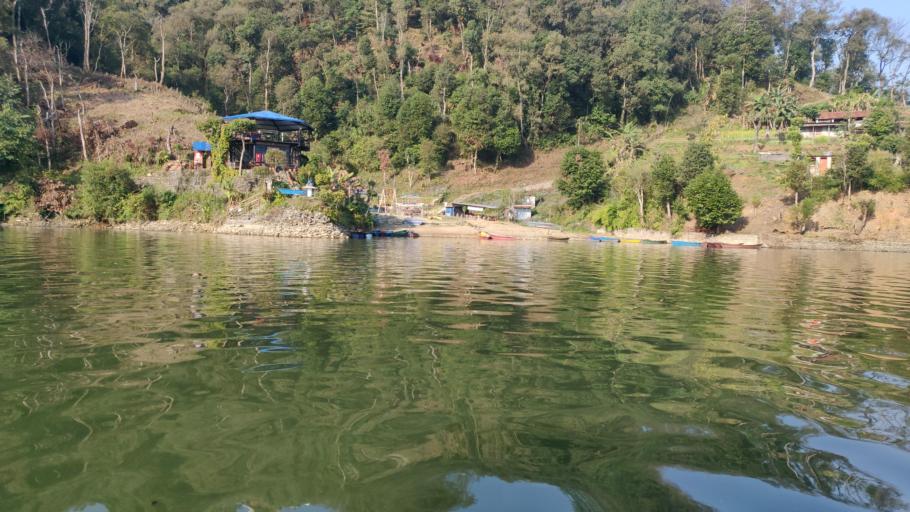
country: NP
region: Western Region
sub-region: Gandaki Zone
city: Pokhara
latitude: 28.2071
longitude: 83.9487
